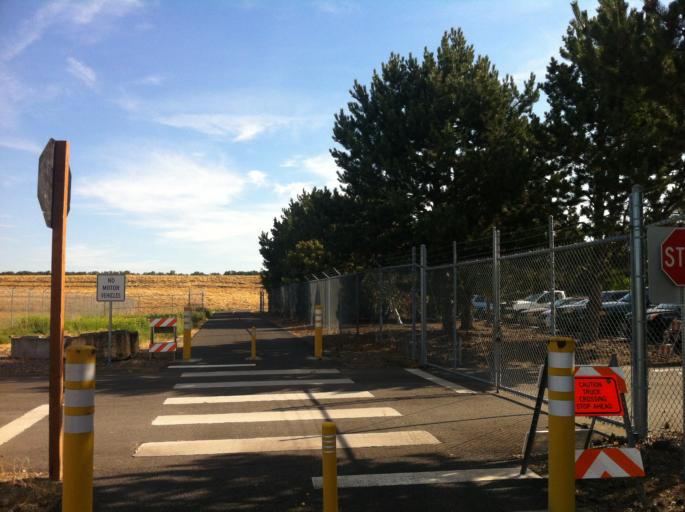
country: US
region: Washington
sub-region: Clark County
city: Orchards
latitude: 45.5799
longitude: -122.5596
